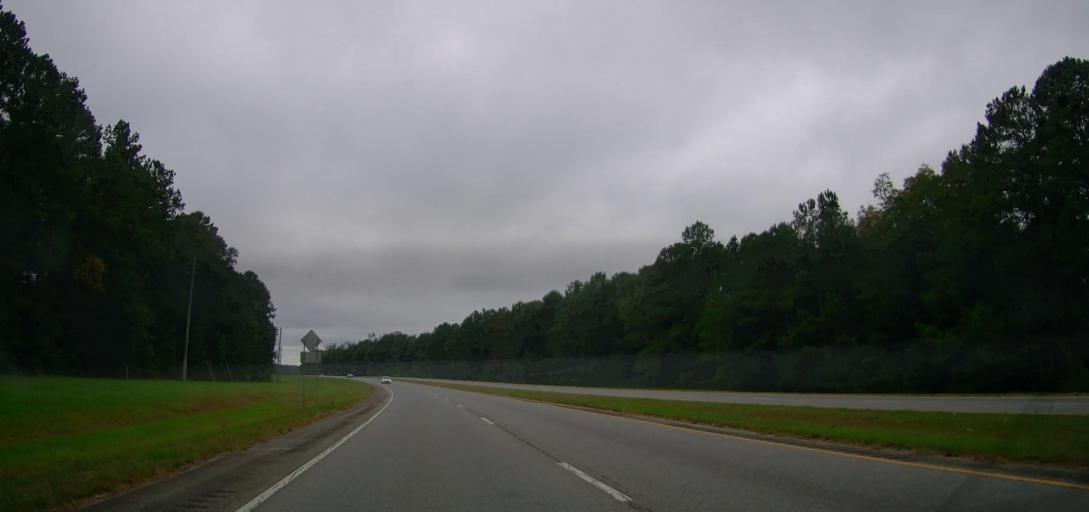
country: US
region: Georgia
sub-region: Thomas County
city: Thomasville
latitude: 30.8587
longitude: -84.0076
